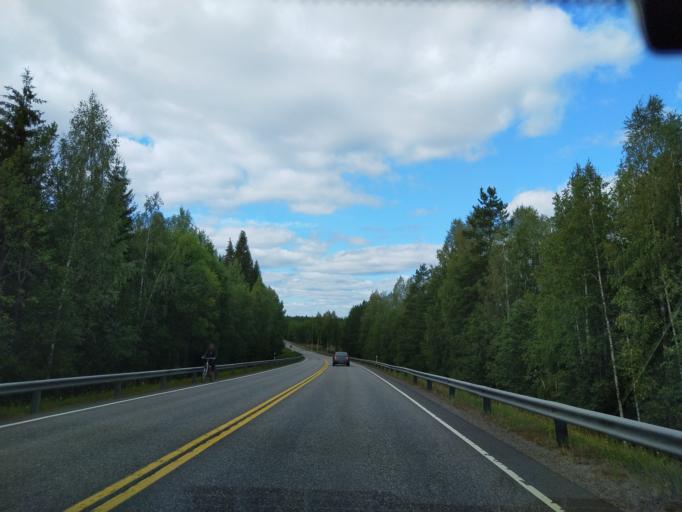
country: FI
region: Haeme
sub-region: Riihimaeki
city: Loppi
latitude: 60.7471
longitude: 24.3402
